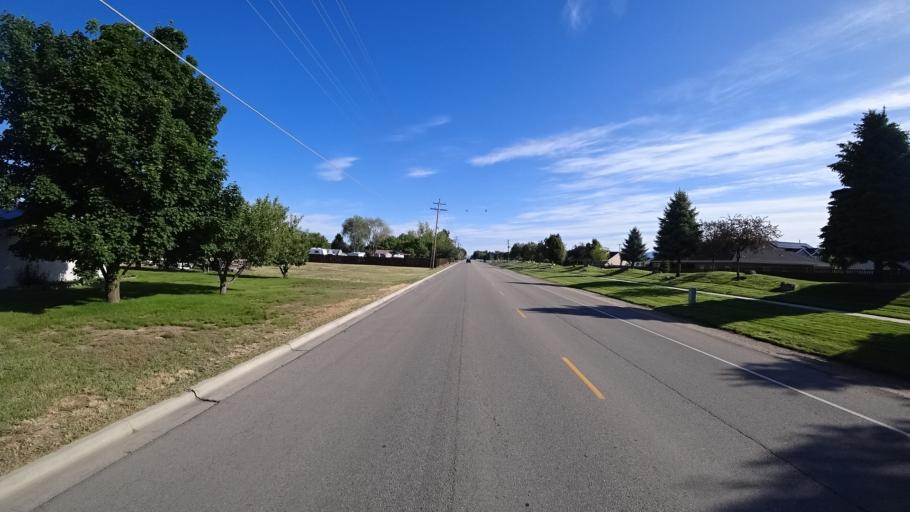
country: US
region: Idaho
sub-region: Ada County
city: Garden City
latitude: 43.5487
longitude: -116.2743
